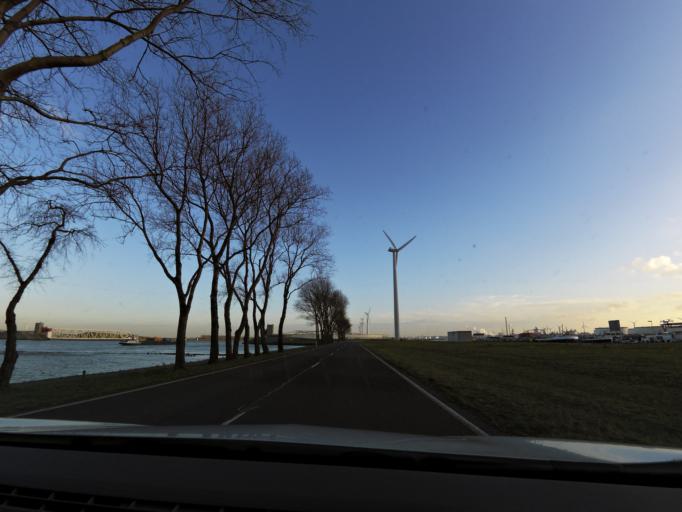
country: NL
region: South Holland
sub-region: Gemeente Rotterdam
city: Hoek van Holland
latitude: 51.9562
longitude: 4.1527
